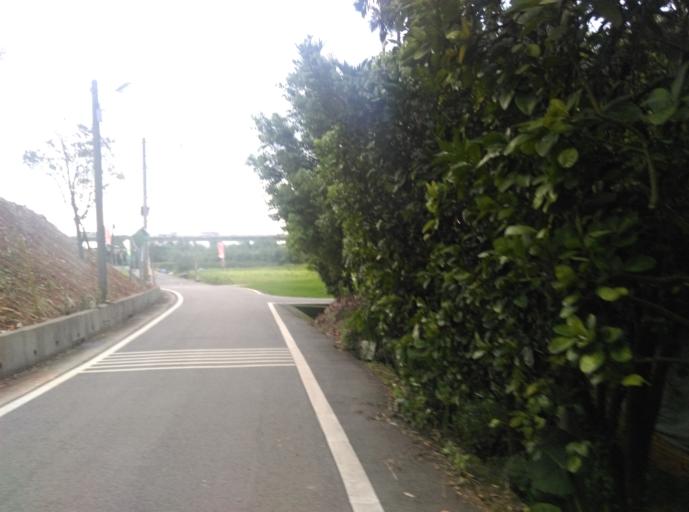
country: TW
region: Taiwan
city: Taoyuan City
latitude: 24.9982
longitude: 121.2523
